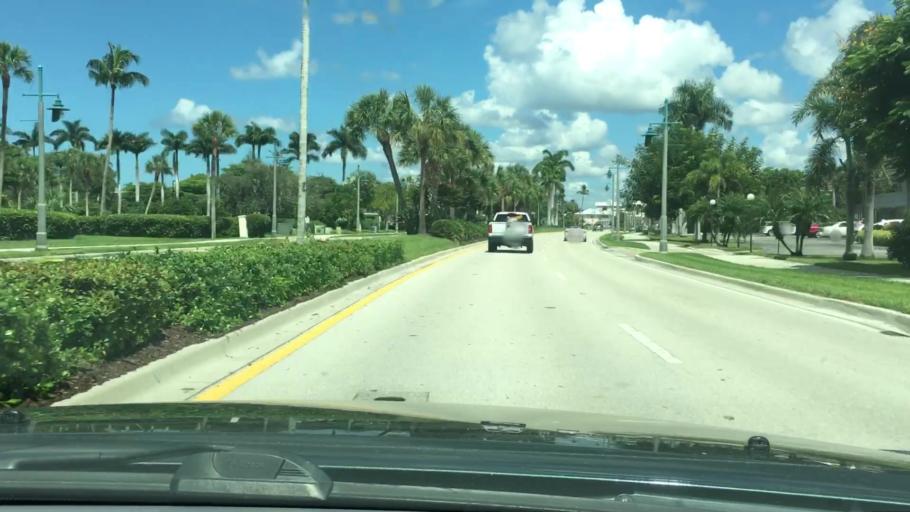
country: US
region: Florida
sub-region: Collier County
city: Marco
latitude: 25.9378
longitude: -81.7324
